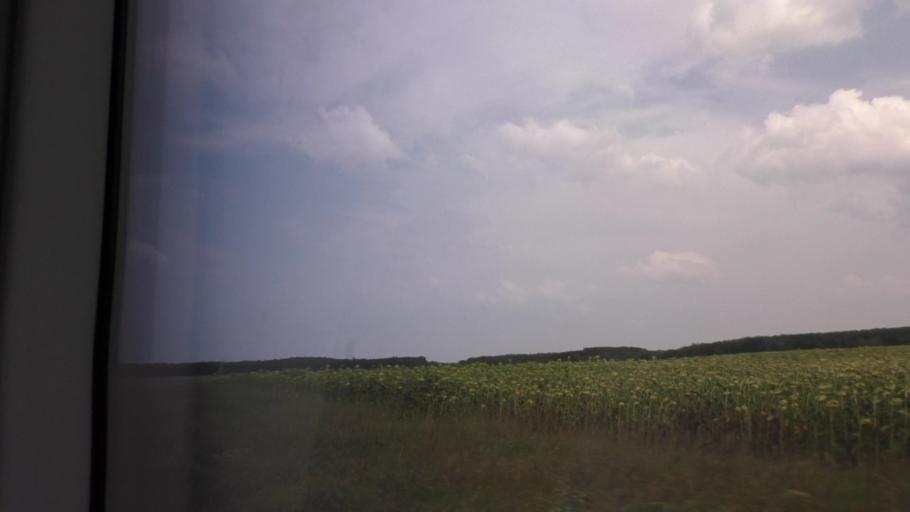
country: DE
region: Brandenburg
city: Mixdorf
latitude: 52.1892
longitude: 14.3891
